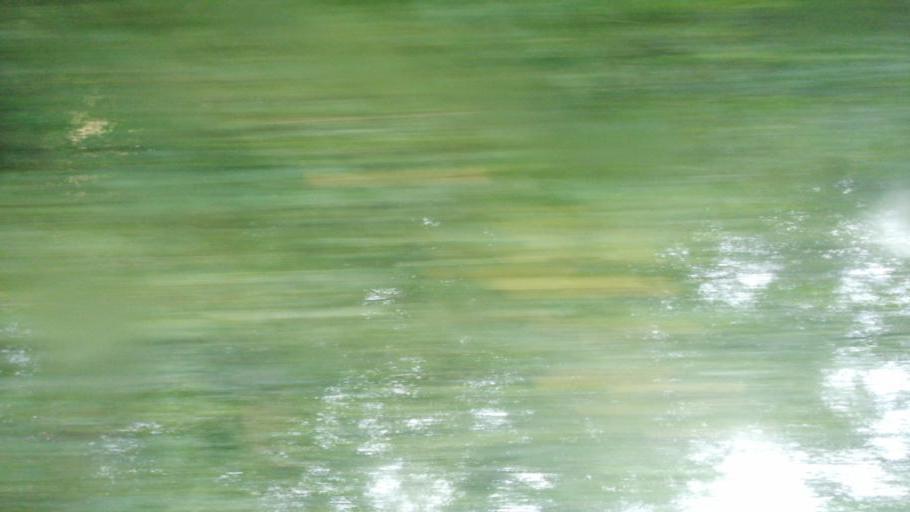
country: GB
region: Scotland
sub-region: Aberdeenshire
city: Huntly
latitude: 57.4095
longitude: -2.7962
